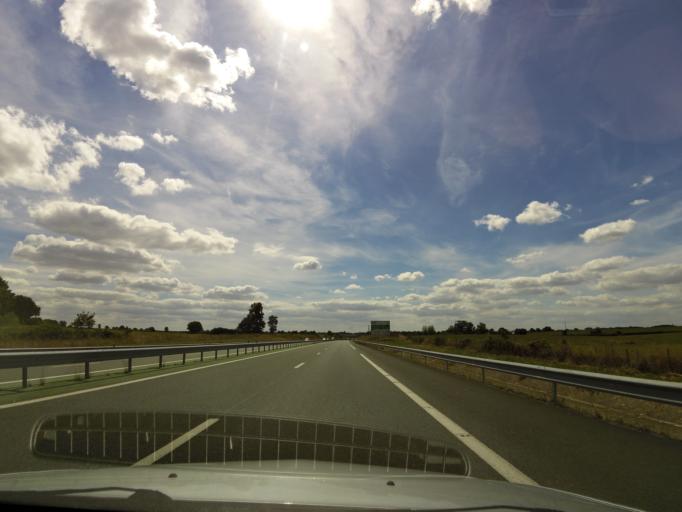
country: FR
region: Pays de la Loire
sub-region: Departement de la Vendee
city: Les Essarts
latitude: 46.8013
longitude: -1.2209
